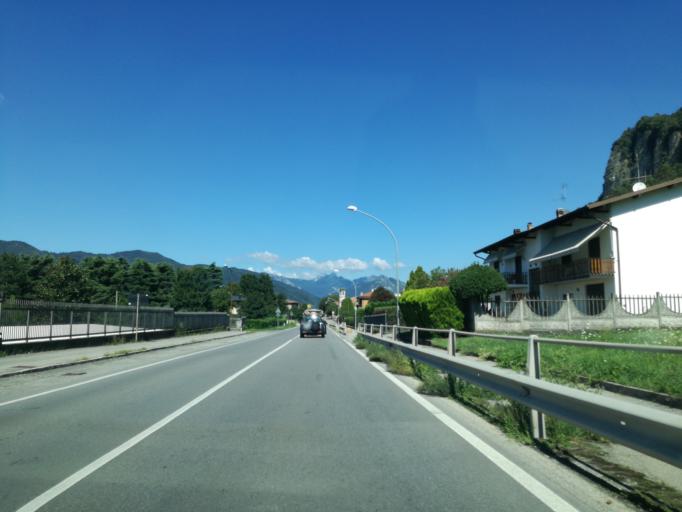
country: IT
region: Lombardy
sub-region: Provincia di Lecco
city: Monte Marenzo
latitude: 45.7595
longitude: 9.4521
